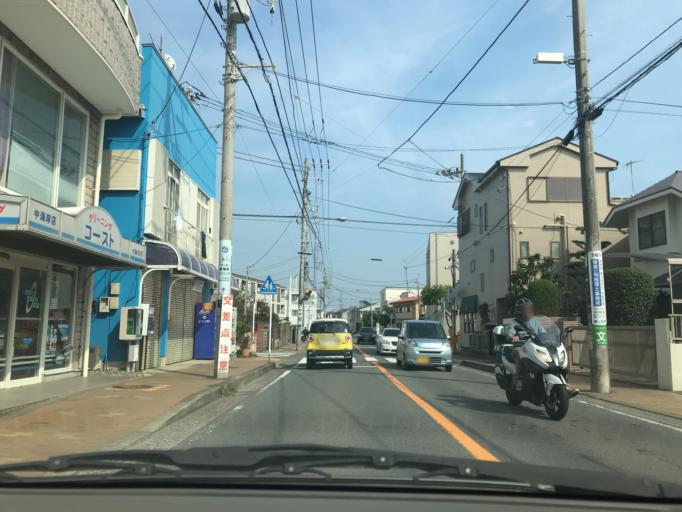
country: JP
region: Kanagawa
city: Chigasaki
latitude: 35.3243
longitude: 139.4019
